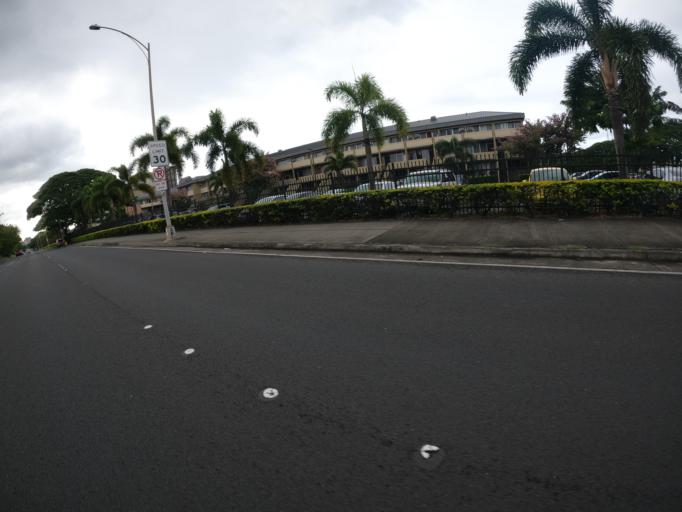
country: US
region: Hawaii
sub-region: Honolulu County
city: Honolulu
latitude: 21.3192
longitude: -157.8616
